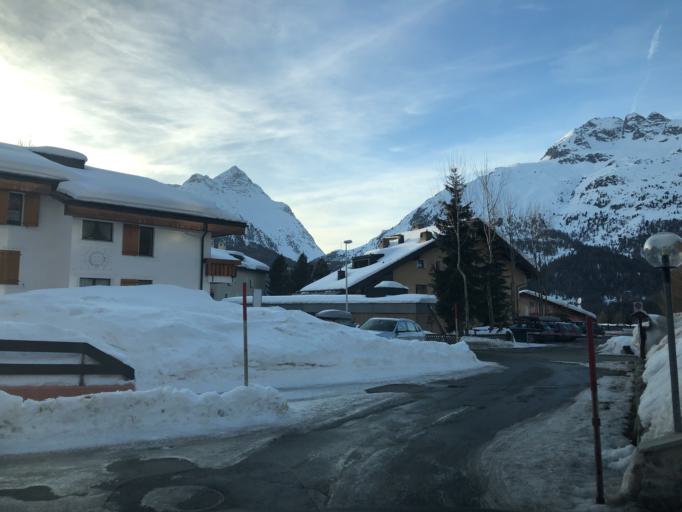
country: CH
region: Grisons
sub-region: Maloja District
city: Silvaplana
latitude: 46.4580
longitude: 9.8136
